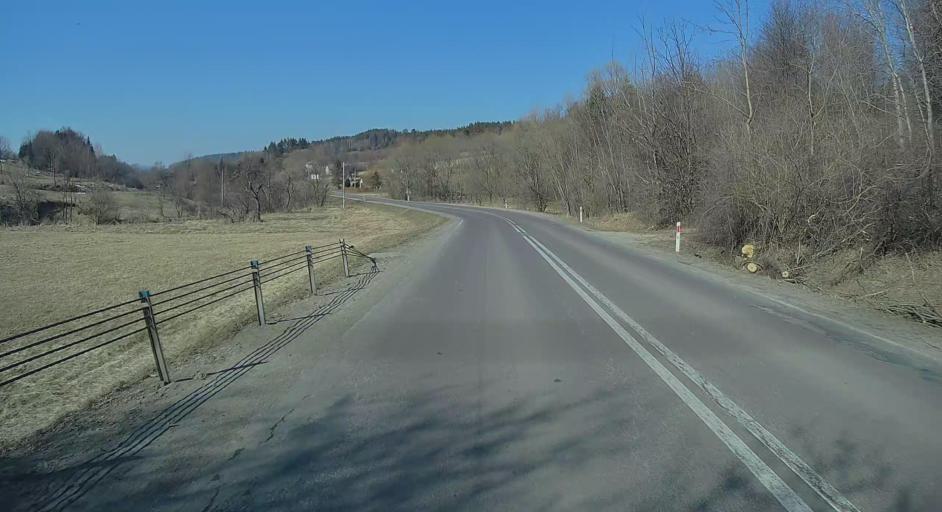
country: PL
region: Subcarpathian Voivodeship
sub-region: Powiat bieszczadzki
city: Ustrzyki Dolne
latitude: 49.5364
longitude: 22.5964
